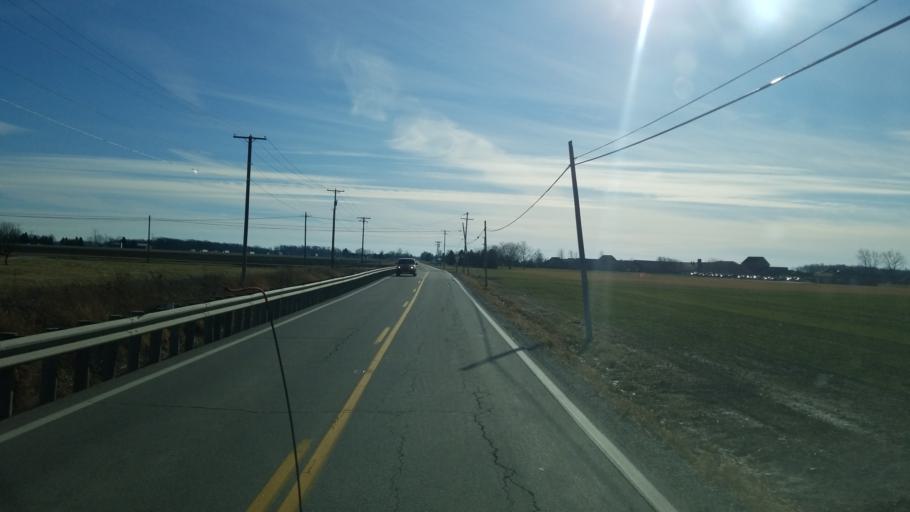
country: US
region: Ohio
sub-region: Wood County
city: Luckey
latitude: 41.4510
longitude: -83.4539
